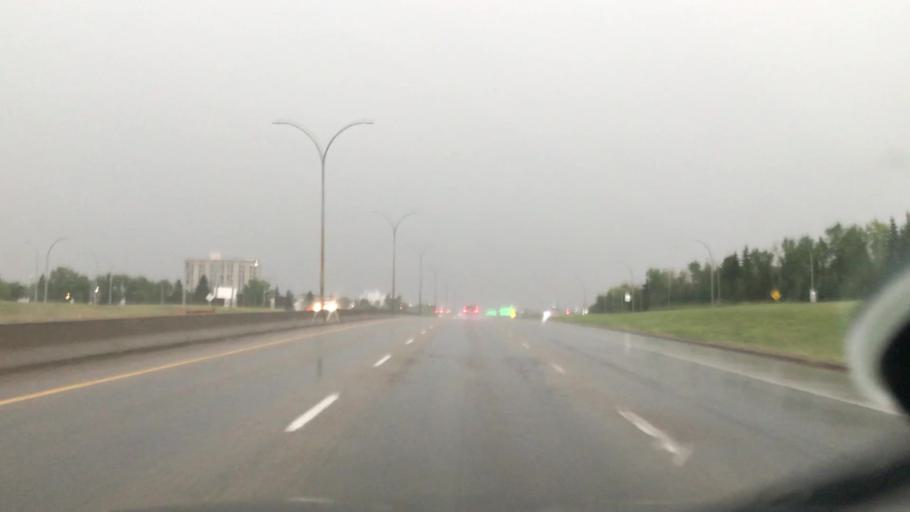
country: CA
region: Alberta
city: Edmonton
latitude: 53.4824
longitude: -113.5130
